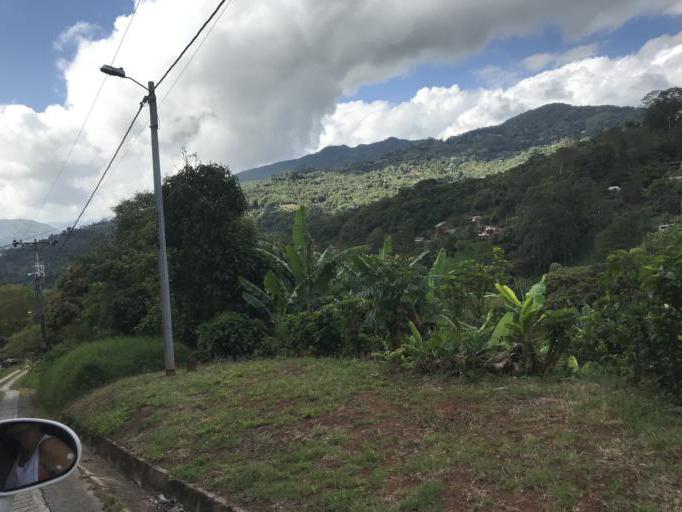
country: CO
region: Valle del Cauca
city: Cali
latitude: 3.5168
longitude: -76.6048
